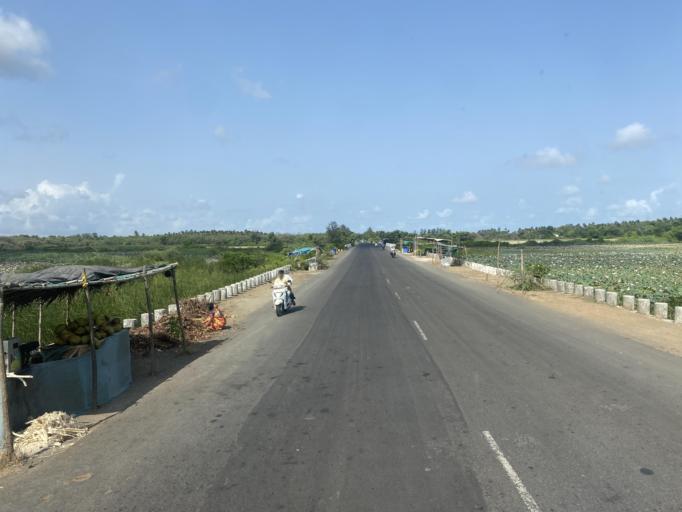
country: IN
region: Daman and Diu
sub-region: Daman District
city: Daman
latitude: 20.3523
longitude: 72.8200
